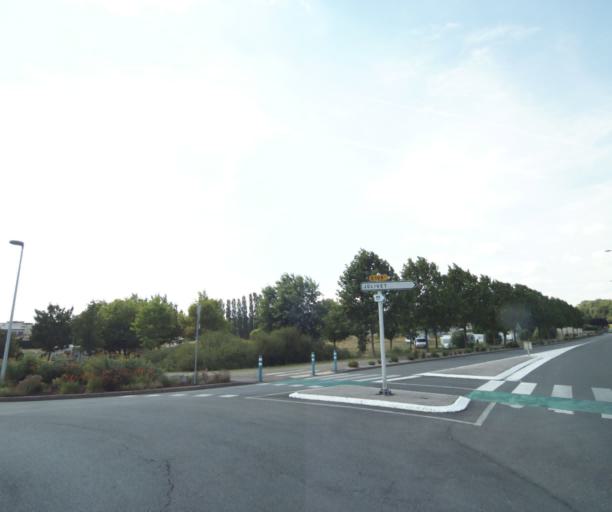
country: FR
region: Lorraine
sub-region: Departement de Meurthe-et-Moselle
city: Luneville
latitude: 48.6013
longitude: 6.4984
